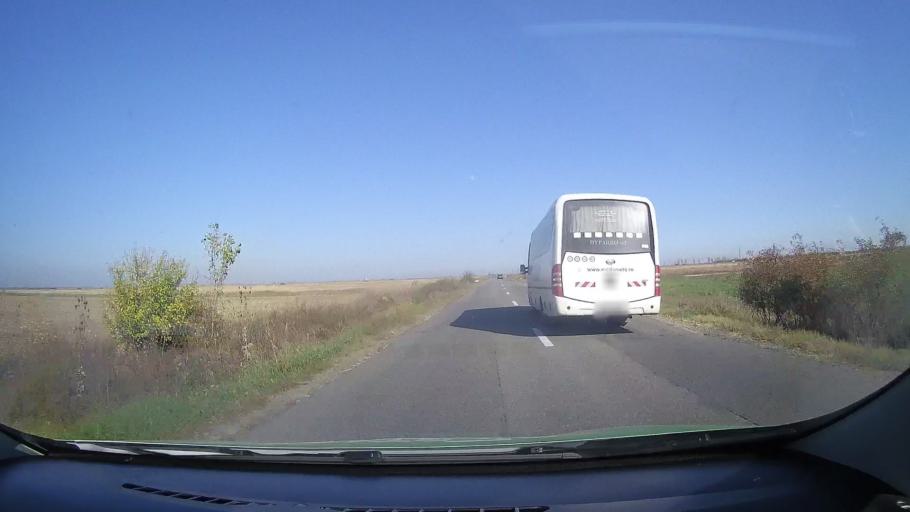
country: RO
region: Satu Mare
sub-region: Comuna Cauas
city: Cauas
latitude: 47.5879
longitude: 22.5471
